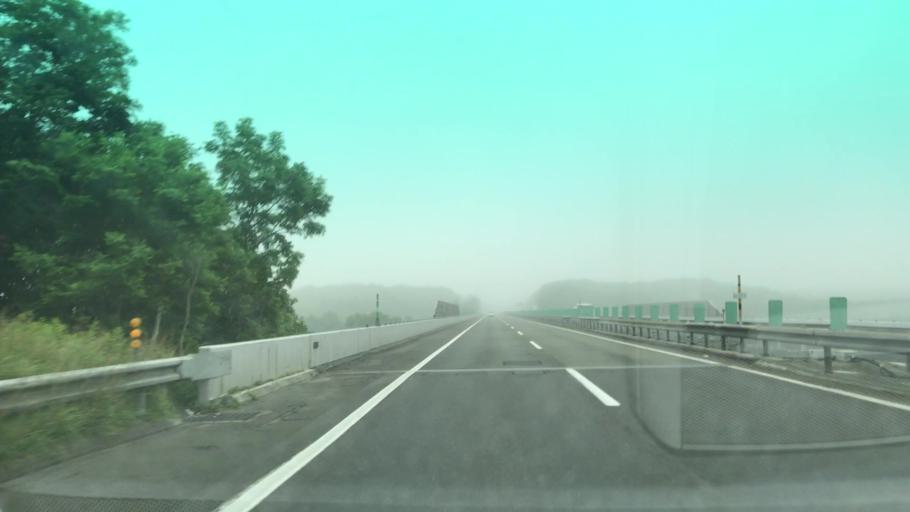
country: JP
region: Hokkaido
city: Chitose
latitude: 42.8081
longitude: 141.6227
